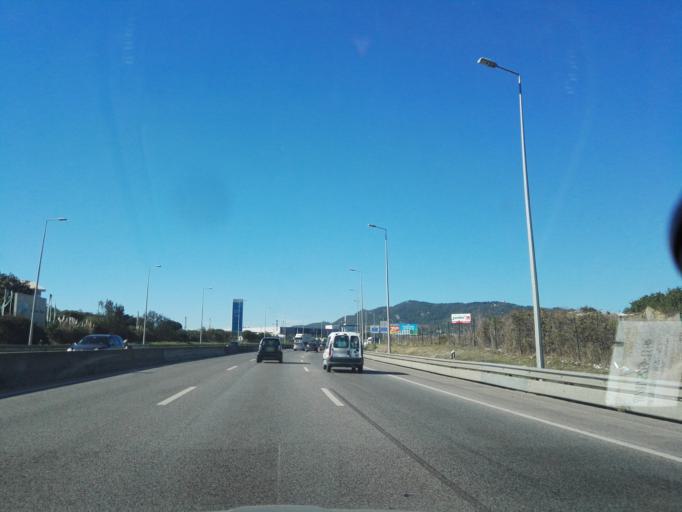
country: PT
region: Lisbon
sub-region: Sintra
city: Rio de Mouro
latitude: 38.7759
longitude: -9.3440
